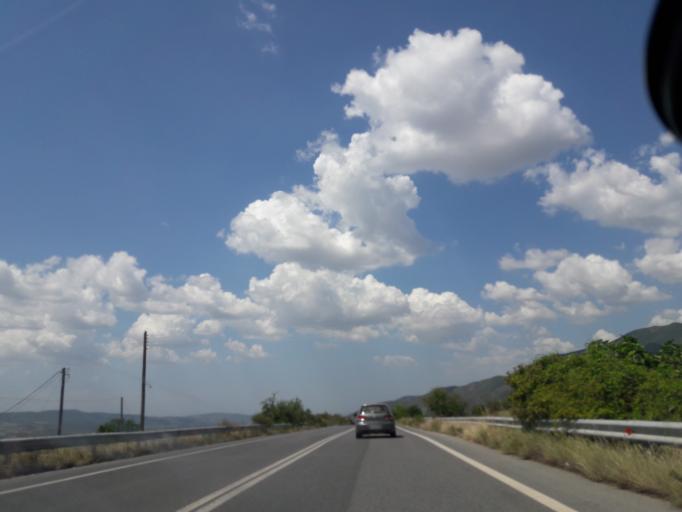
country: GR
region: Central Macedonia
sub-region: Nomos Chalkidikis
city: Galatista
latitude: 40.4635
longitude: 23.2689
